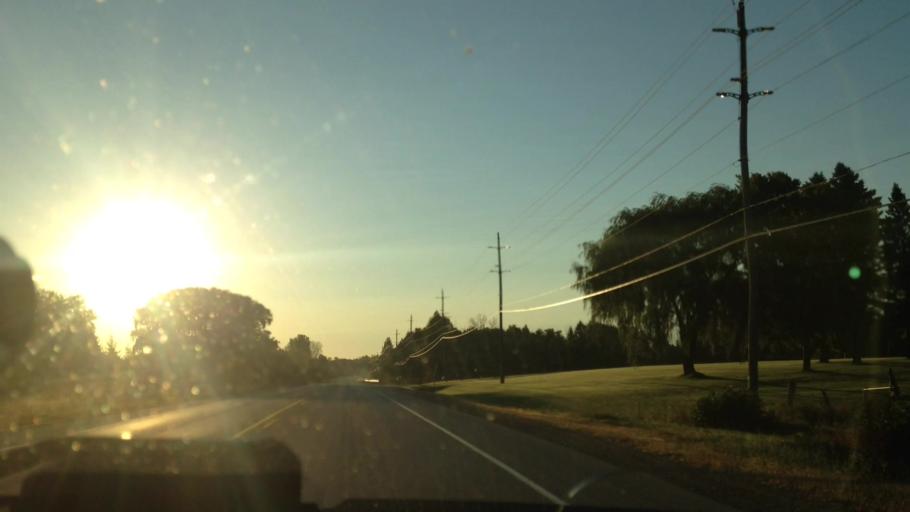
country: US
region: Wisconsin
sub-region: Washington County
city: Newburg
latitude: 43.4085
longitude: -88.0029
